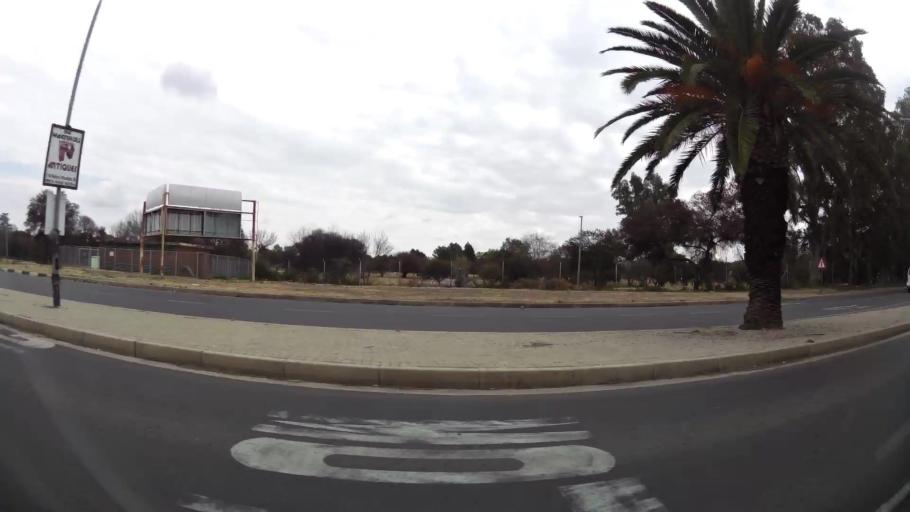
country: ZA
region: Orange Free State
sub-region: Mangaung Metropolitan Municipality
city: Bloemfontein
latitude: -29.0975
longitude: 26.2034
